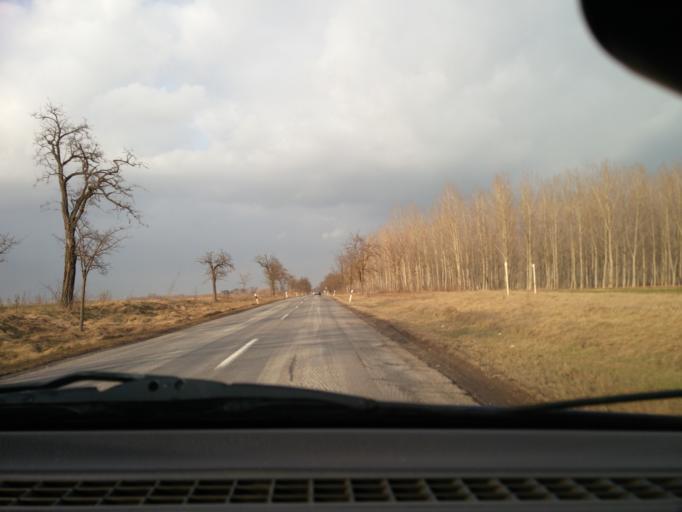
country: HU
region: Pest
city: Tapioszolos
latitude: 47.3025
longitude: 19.8703
